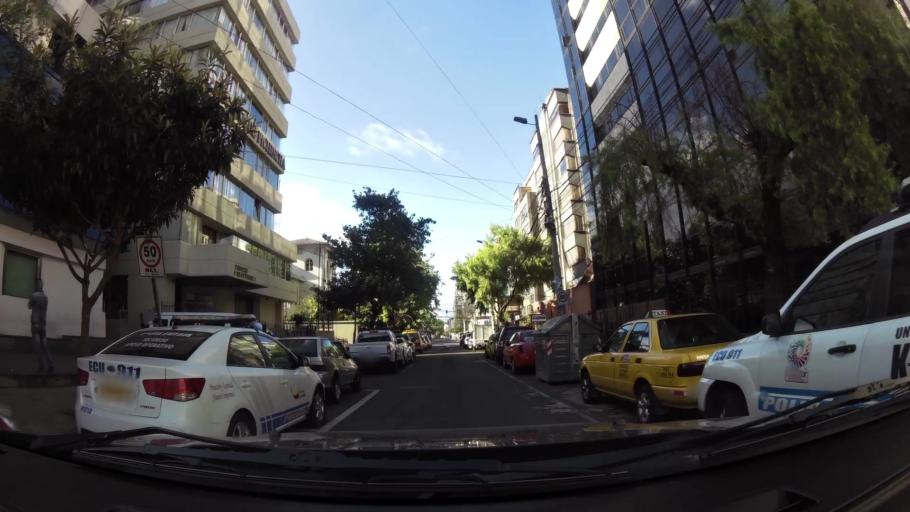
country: EC
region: Pichincha
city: Quito
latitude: -0.2071
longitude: -78.4978
